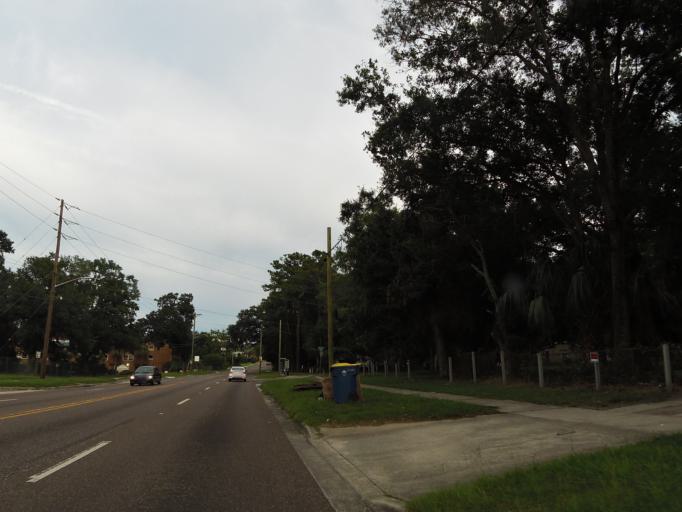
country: US
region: Florida
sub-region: Duval County
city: Jacksonville
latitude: 30.3713
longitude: -81.6859
